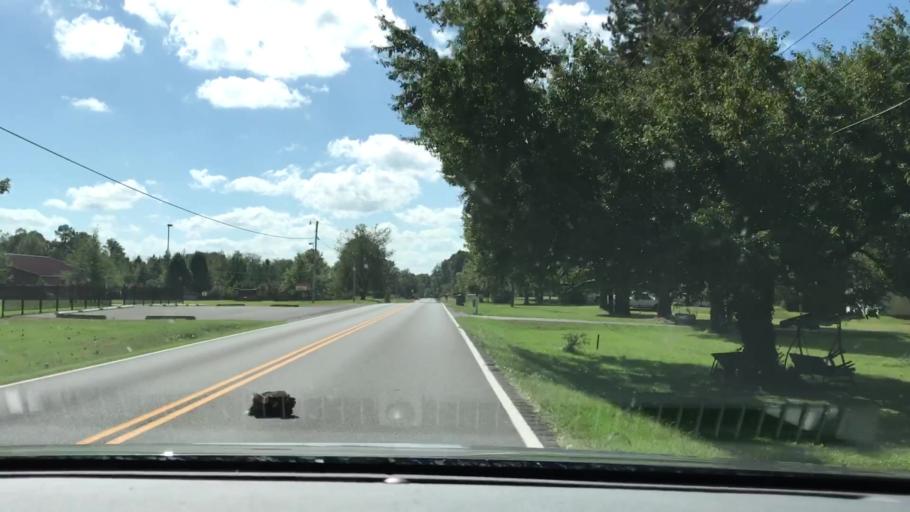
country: US
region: Kentucky
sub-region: McCracken County
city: Reidland
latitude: 36.9174
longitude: -88.5205
